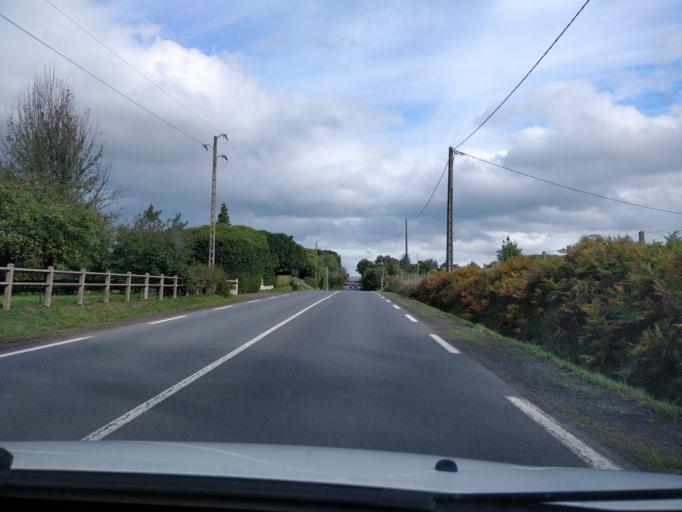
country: FR
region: Lower Normandy
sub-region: Departement du Calvados
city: Saint-Sever-Calvados
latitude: 48.8391
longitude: -1.0118
